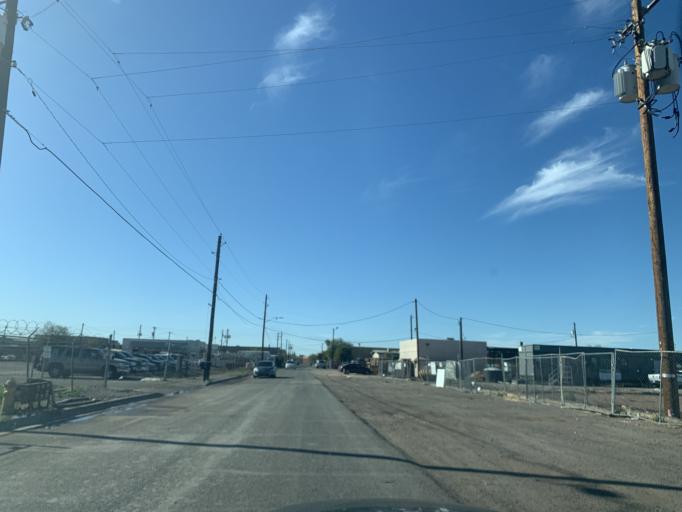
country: US
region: Arizona
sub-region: Maricopa County
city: Tempe Junction
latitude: 33.4183
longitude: -111.9975
